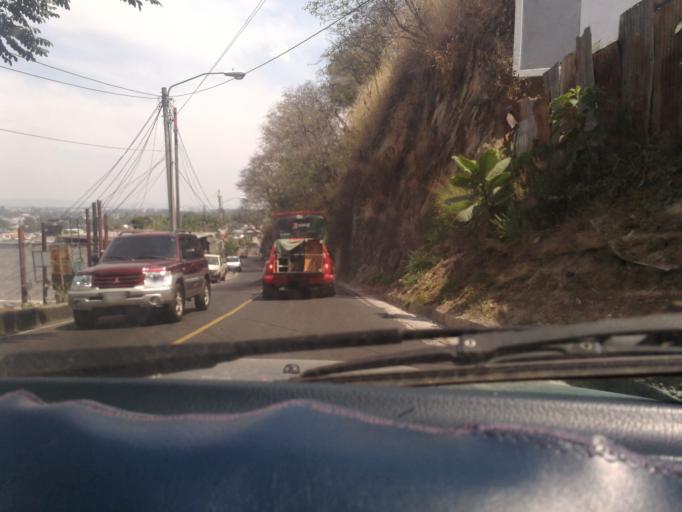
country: GT
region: Guatemala
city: Guatemala City
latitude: 14.6203
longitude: -90.4760
